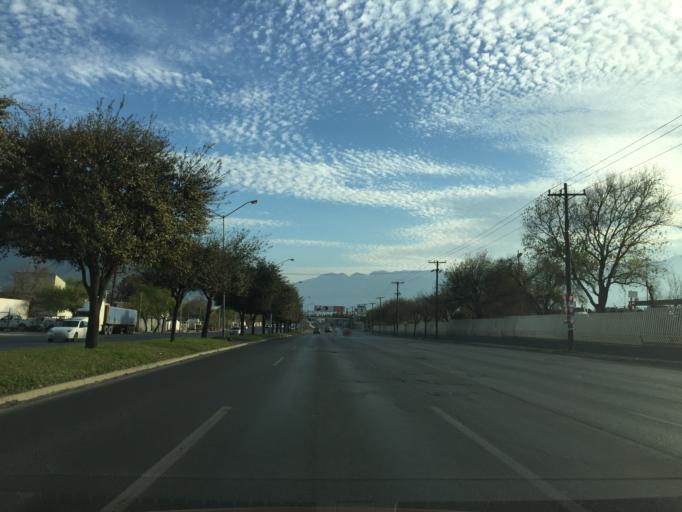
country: MX
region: Nuevo Leon
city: Guadalupe
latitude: 25.6978
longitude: -100.2683
